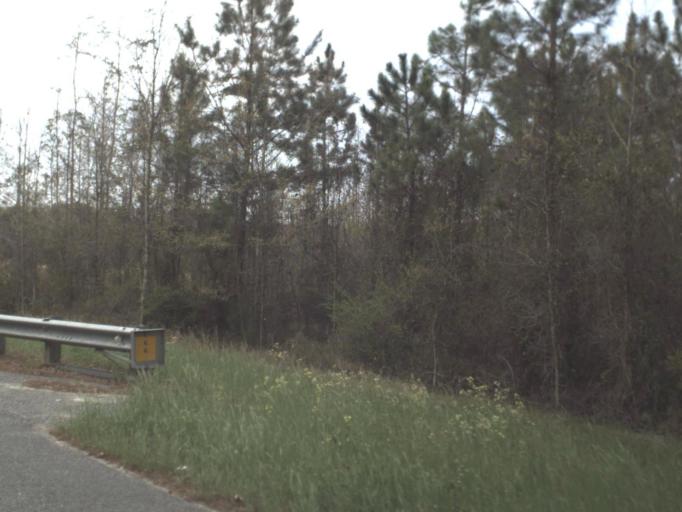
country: US
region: Florida
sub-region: Holmes County
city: Bonifay
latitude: 30.8614
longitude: -85.6665
